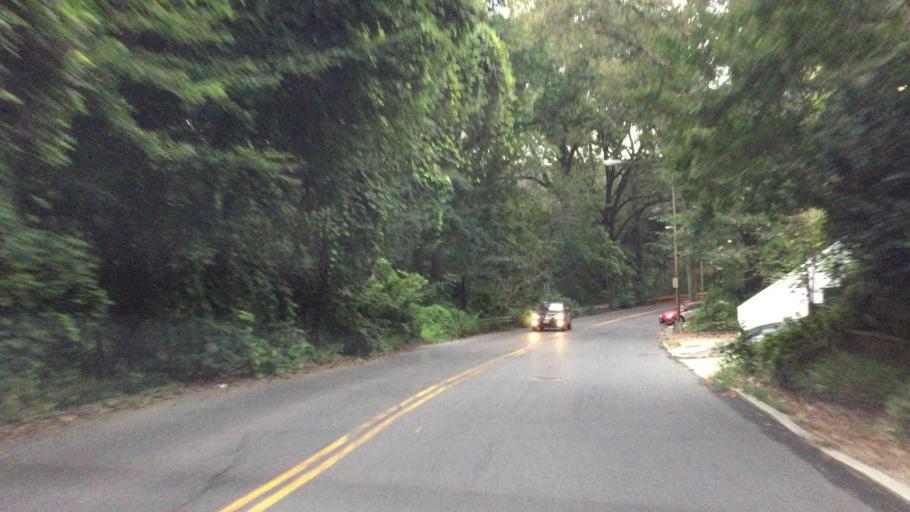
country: US
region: Washington, D.C.
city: Washington, D.C.
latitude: 38.9247
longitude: -77.0499
